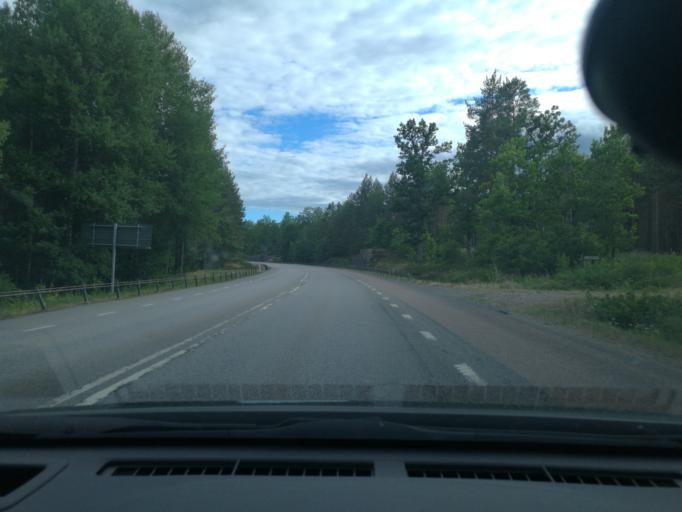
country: SE
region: Kalmar
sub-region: Vasterviks Kommun
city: Ankarsrum
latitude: 57.6538
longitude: 16.4414
